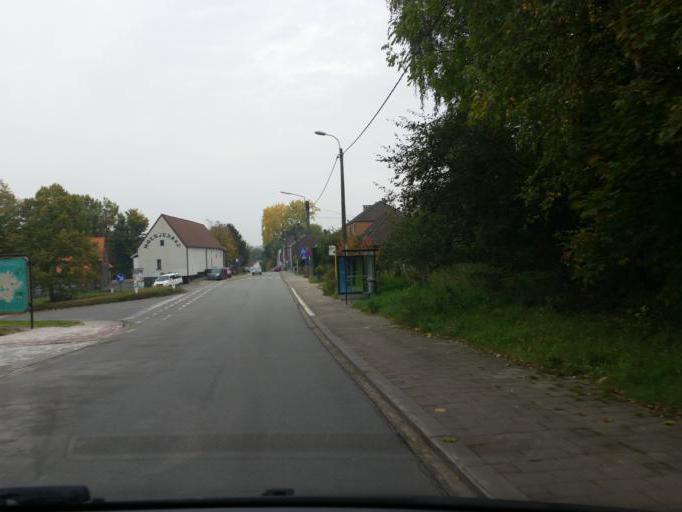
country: BE
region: Flanders
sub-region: Provincie Vlaams-Brabant
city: Drogenbos
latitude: 50.7742
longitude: 4.3167
